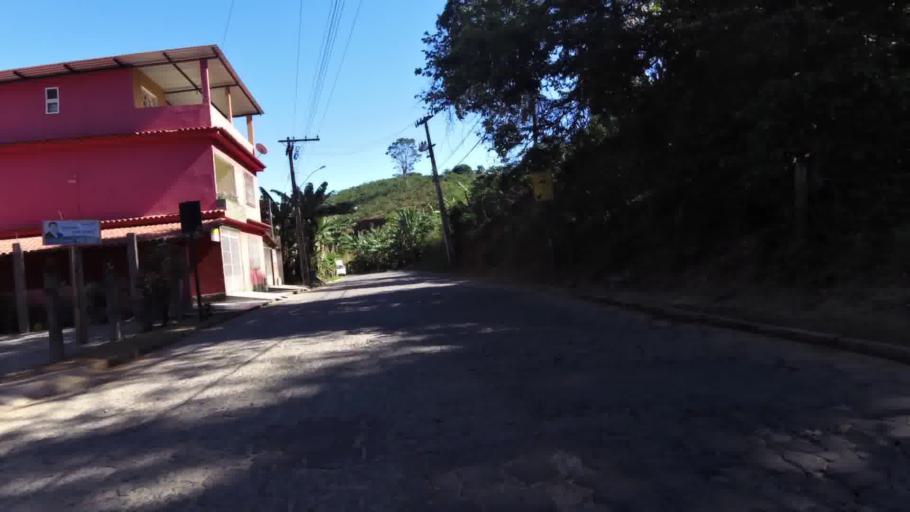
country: BR
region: Espirito Santo
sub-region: Iconha
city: Iconha
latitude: -20.7870
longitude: -40.8215
